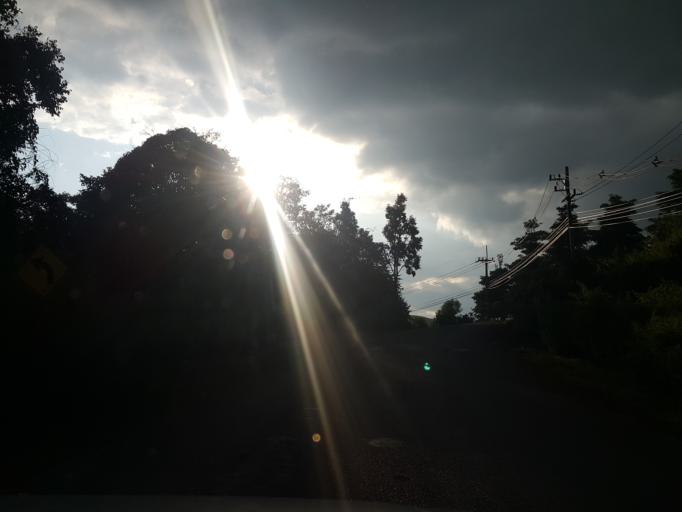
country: TH
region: Chiang Mai
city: Mae Chaem
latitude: 18.7451
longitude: 98.2147
